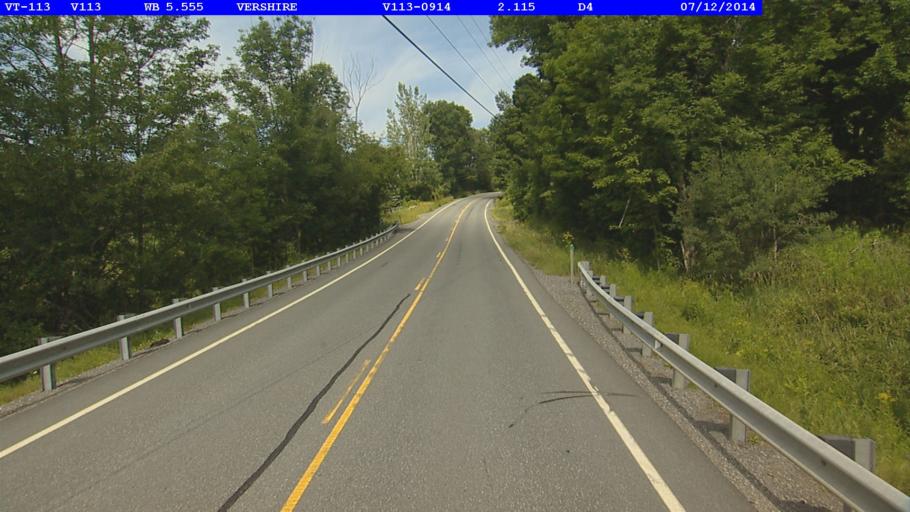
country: US
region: Vermont
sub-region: Orange County
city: Chelsea
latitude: 43.9759
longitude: -72.3495
